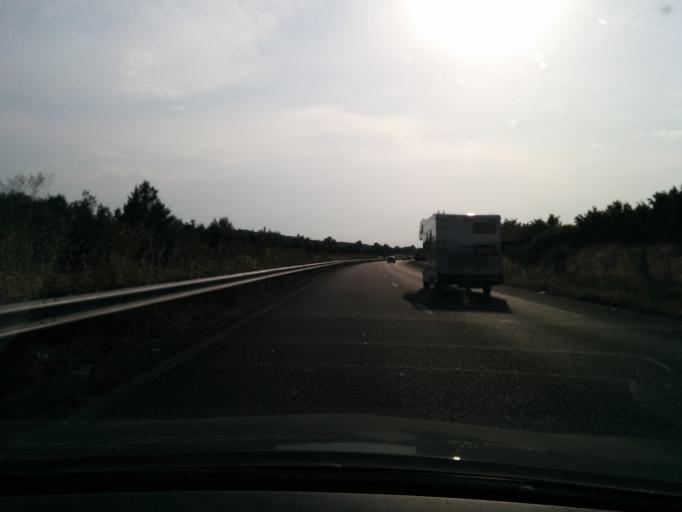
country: FR
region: Midi-Pyrenees
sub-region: Departement du Tarn
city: Saint-Sulpice-la-Pointe
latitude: 43.7531
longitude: 1.6949
